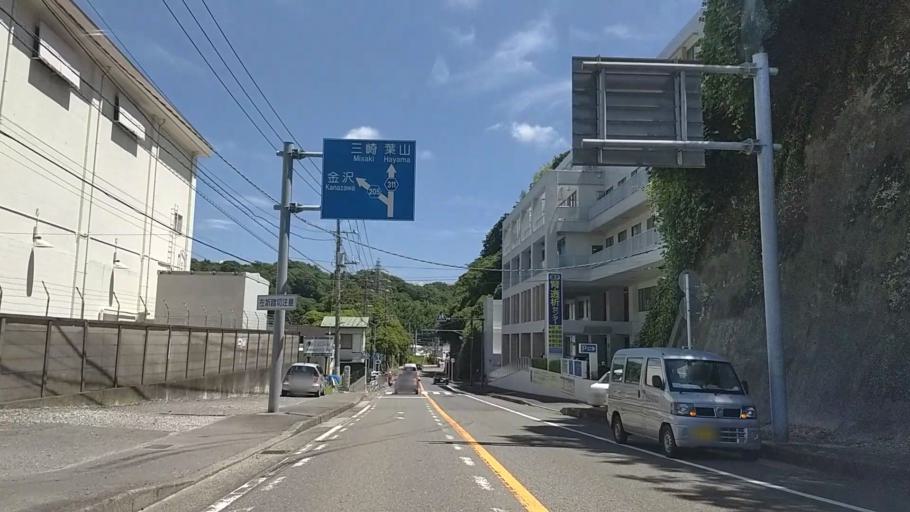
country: JP
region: Kanagawa
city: Kamakura
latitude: 35.3063
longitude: 139.5671
